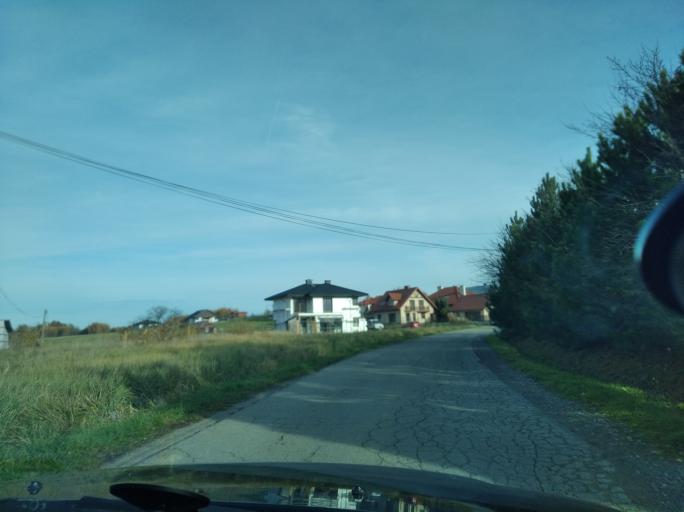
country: PL
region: Subcarpathian Voivodeship
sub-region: Powiat rzeszowski
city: Krasne
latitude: 50.0141
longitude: 22.0974
